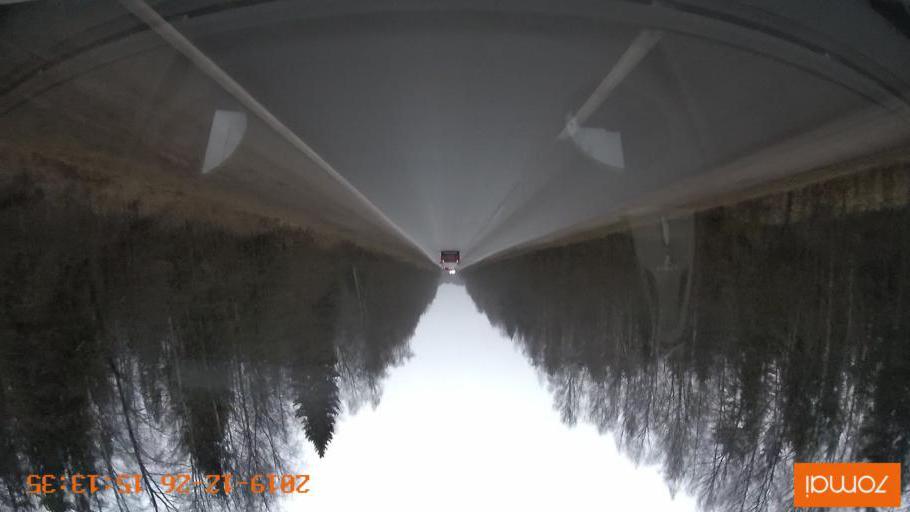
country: RU
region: Jaroslavl
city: Rybinsk
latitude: 58.1150
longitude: 38.8831
